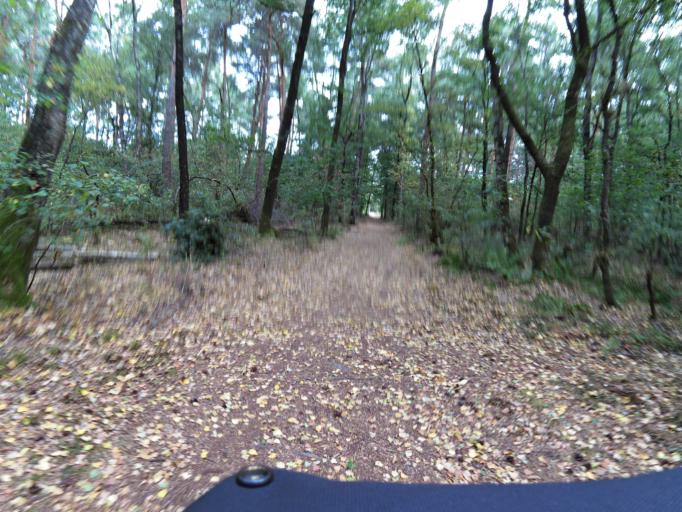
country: NL
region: Limburg
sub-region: Gemeente Bergen
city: Wellerlooi
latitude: 51.5618
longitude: 6.1052
